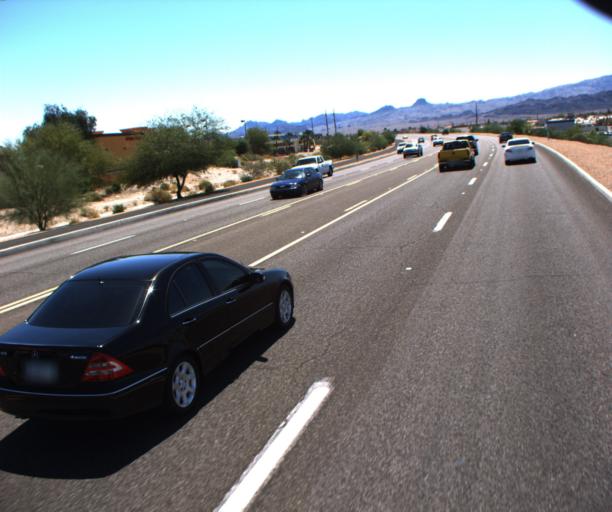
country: US
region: Arizona
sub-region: Mohave County
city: Lake Havasu City
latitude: 34.4806
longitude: -114.3494
